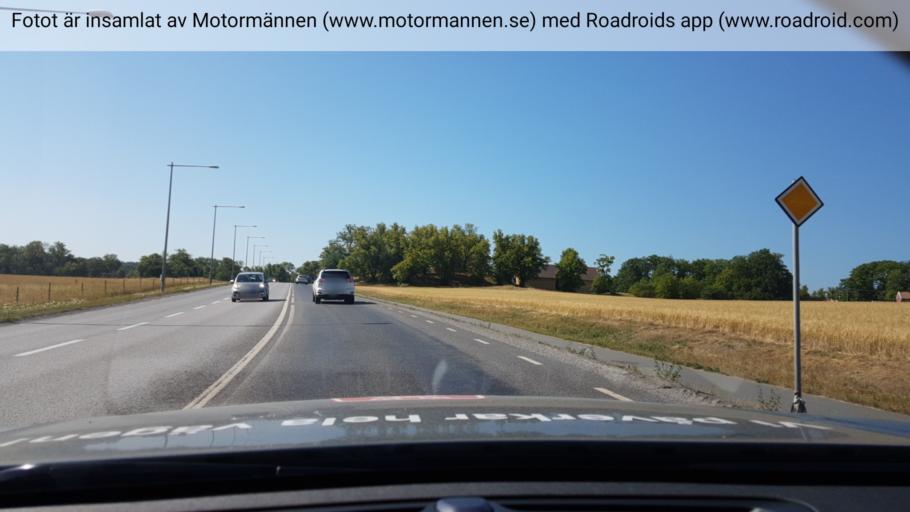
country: SE
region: Stockholm
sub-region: Ekero Kommun
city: Ekeroe
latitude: 59.3242
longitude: 17.8689
